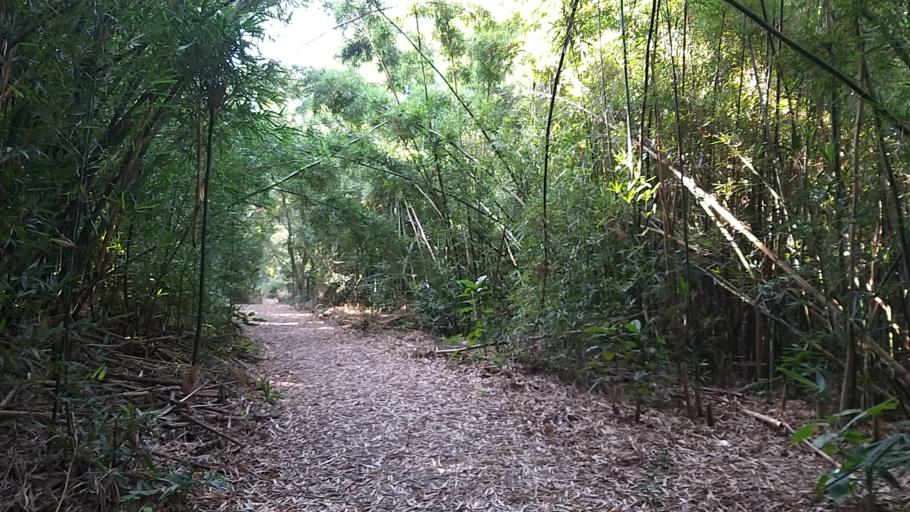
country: HK
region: Tuen Mun
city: Tuen Mun
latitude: 22.4045
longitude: 113.9659
